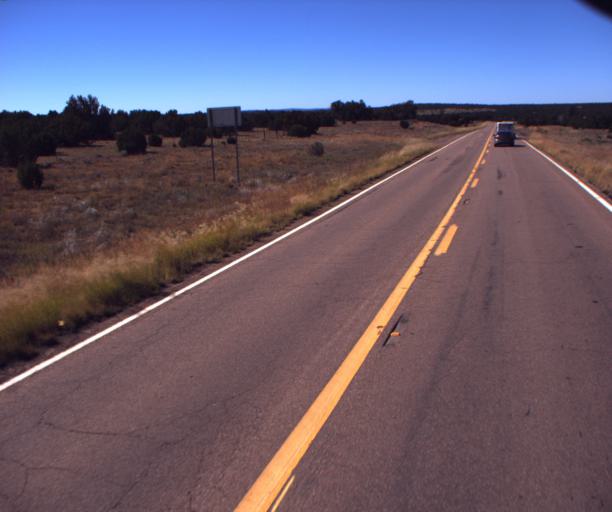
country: US
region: Arizona
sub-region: Navajo County
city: Heber-Overgaard
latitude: 34.4633
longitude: -110.4788
